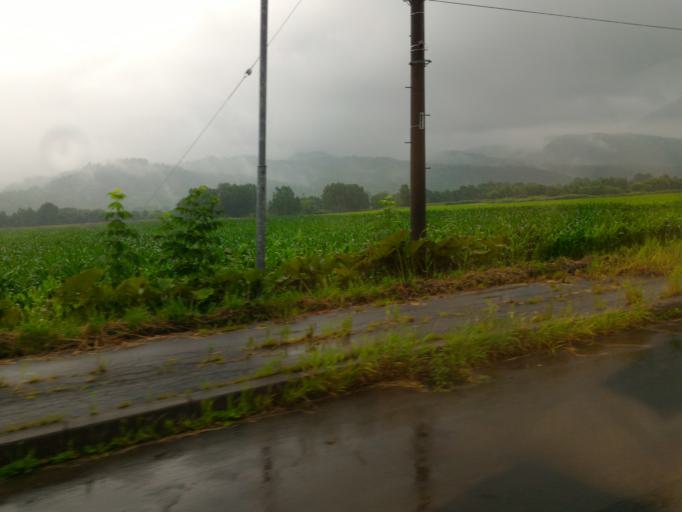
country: JP
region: Hokkaido
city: Nayoro
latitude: 44.5855
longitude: 142.3072
